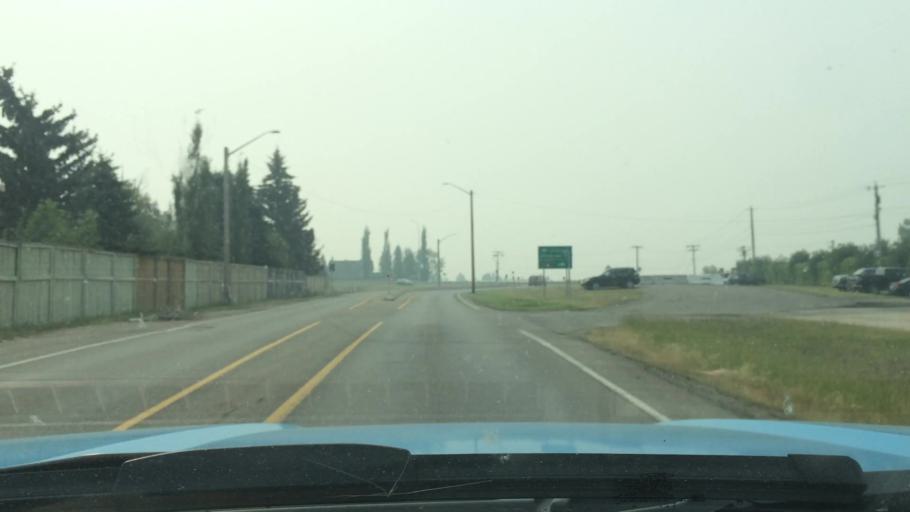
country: CA
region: Alberta
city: Calgary
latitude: 50.9419
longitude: -114.0945
